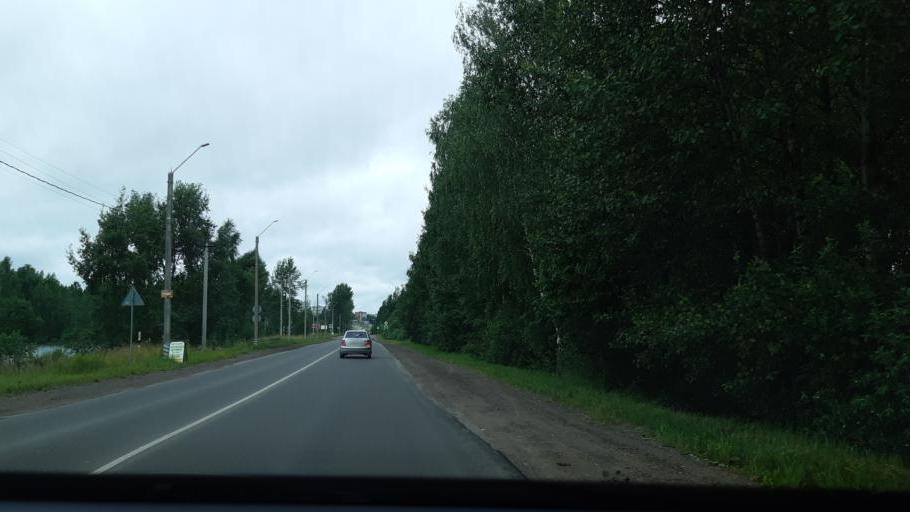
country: RU
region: Smolensk
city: Desnogorsk
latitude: 54.1342
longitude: 33.2773
